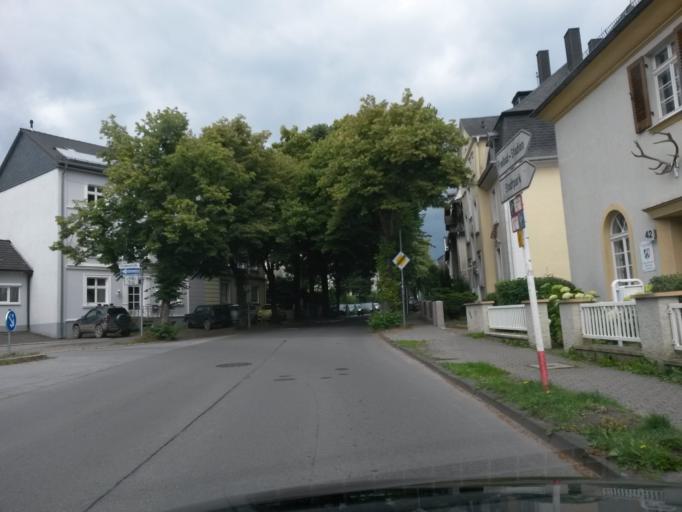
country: DE
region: North Rhine-Westphalia
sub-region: Regierungsbezirk Arnsberg
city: Luedenscheid
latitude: 51.2203
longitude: 7.6170
